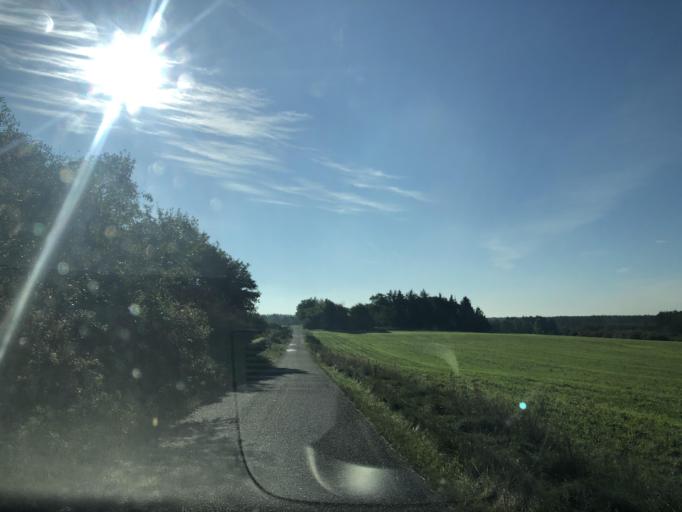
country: DK
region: Central Jutland
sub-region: Holstebro Kommune
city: Holstebro
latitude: 56.3110
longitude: 8.5042
